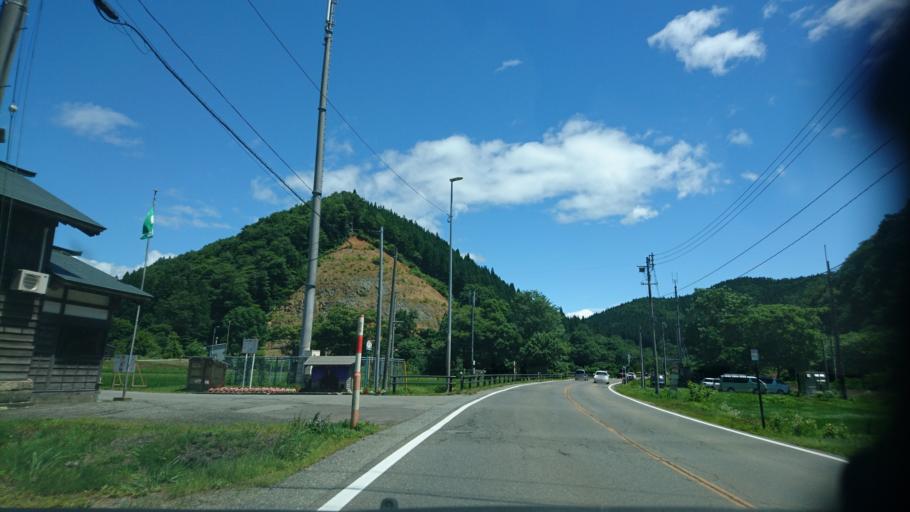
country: JP
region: Akita
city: Kakunodatemachi
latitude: 39.6508
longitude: 140.6674
